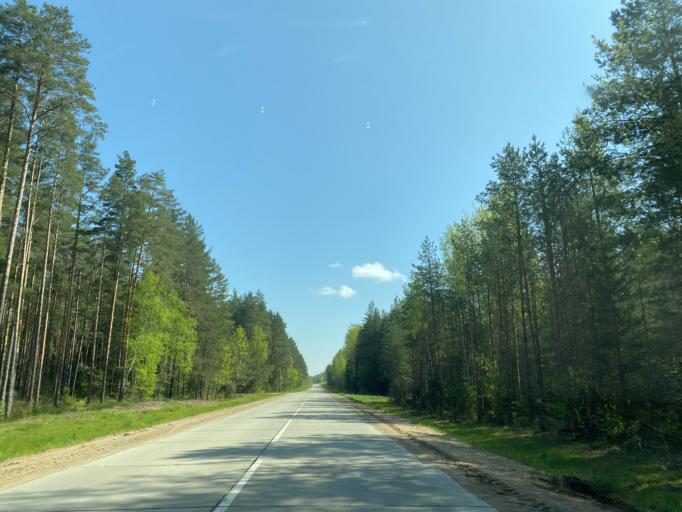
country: BY
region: Minsk
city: Horad Barysaw
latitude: 54.1731
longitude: 28.5256
